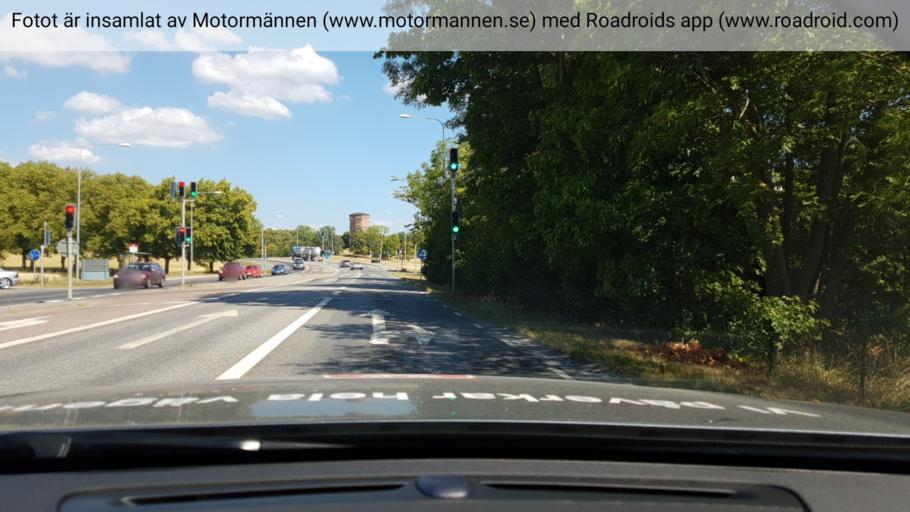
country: SE
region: Stockholm
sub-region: Ekero Kommun
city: Ekeroe
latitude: 59.3194
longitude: 17.8664
